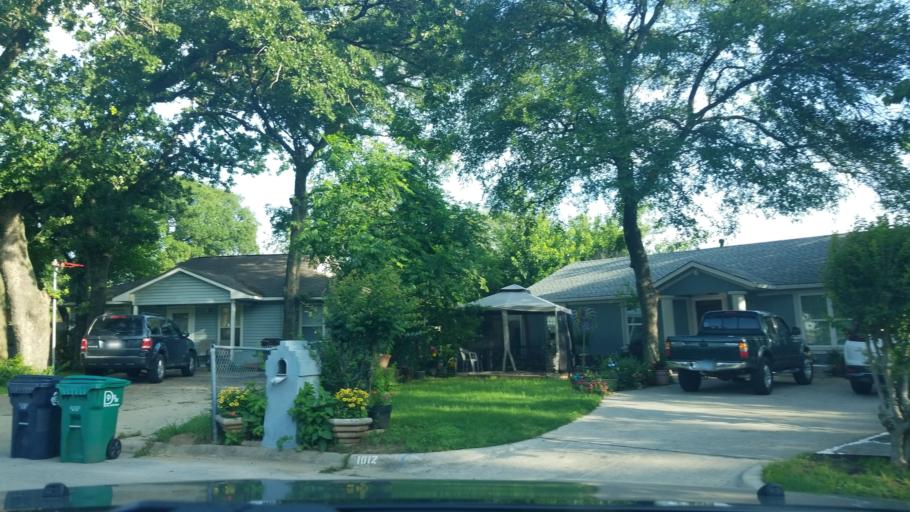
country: US
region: Texas
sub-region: Denton County
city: Denton
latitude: 33.2030
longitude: -97.1170
